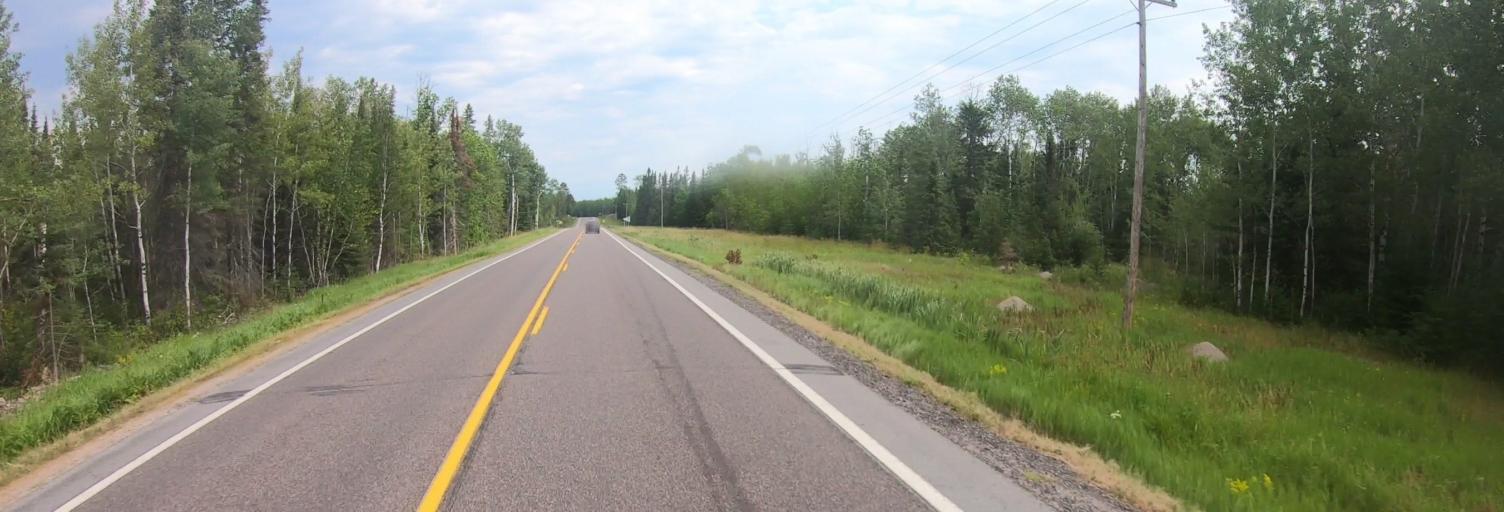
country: US
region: Minnesota
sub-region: Saint Louis County
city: Mountain Iron
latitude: 47.9078
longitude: -92.6577
